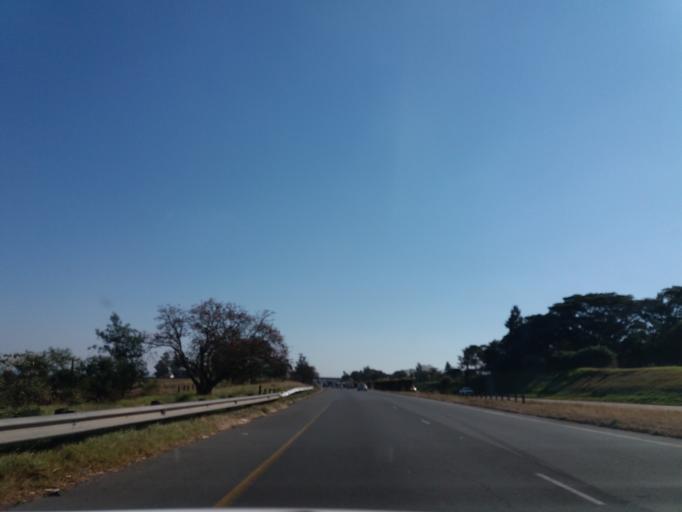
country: ZA
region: KwaZulu-Natal
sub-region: uMgungundlovu District Municipality
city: Camperdown
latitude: -29.7306
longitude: 30.5607
